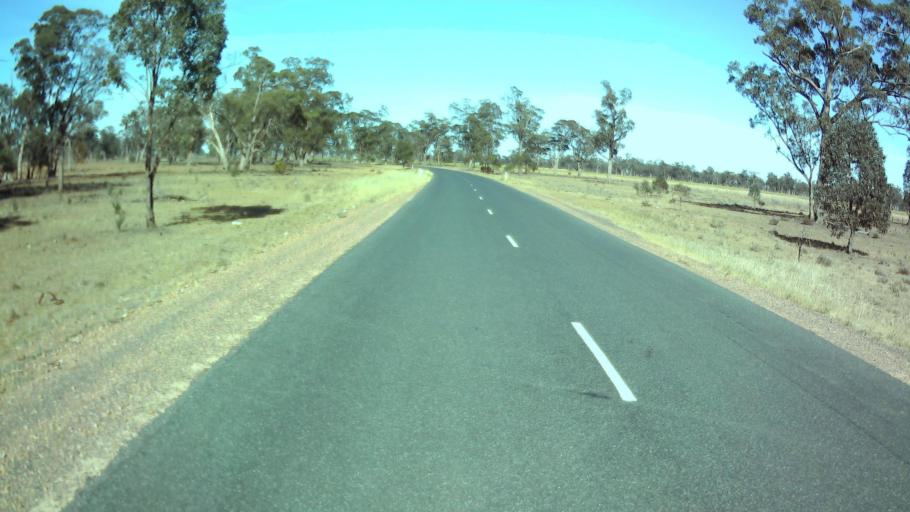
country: AU
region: New South Wales
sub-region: Weddin
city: Grenfell
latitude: -34.1137
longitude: 147.8269
